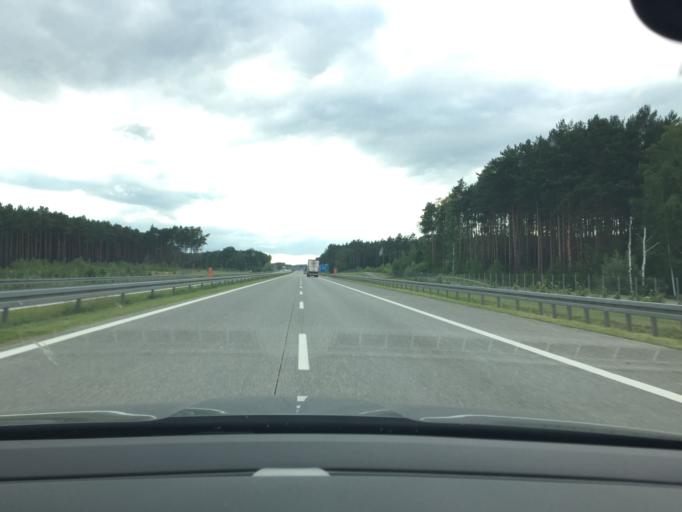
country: PL
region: Lubusz
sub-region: Powiat miedzyrzecki
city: Trzciel
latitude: 52.3293
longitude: 15.8902
